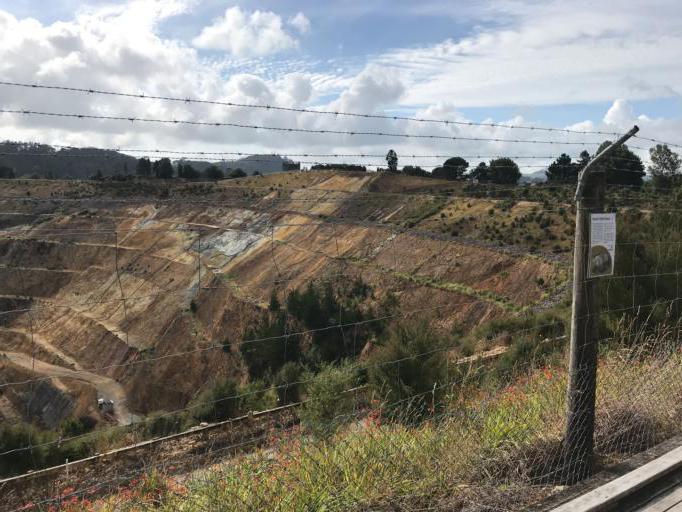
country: NZ
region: Waikato
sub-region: Hauraki District
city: Waihi
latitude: -37.3868
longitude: 175.8382
